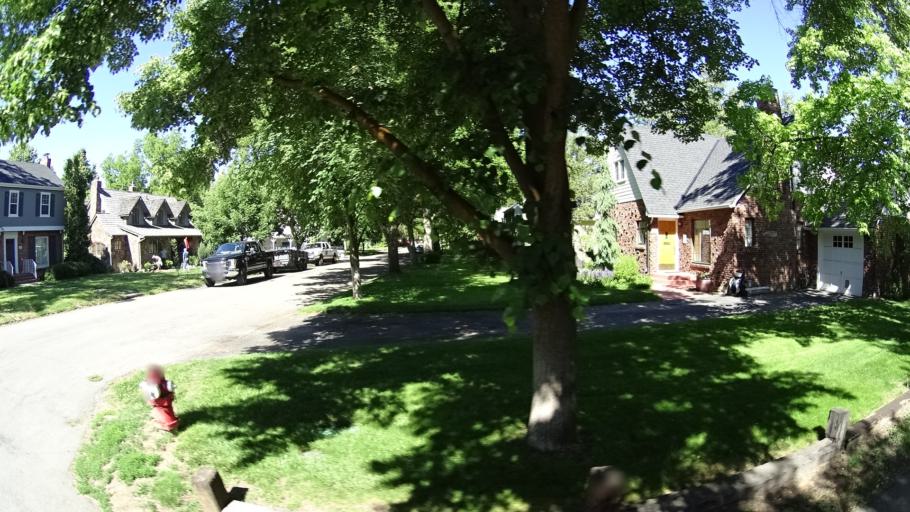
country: US
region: Idaho
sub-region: Ada County
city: Boise
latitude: 43.6374
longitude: -116.2134
